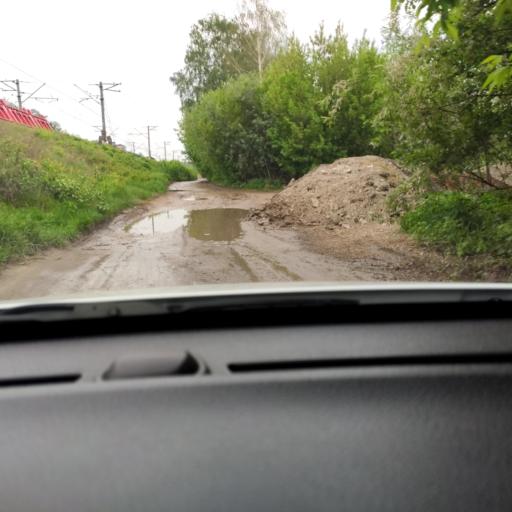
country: RU
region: Tatarstan
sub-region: Gorod Kazan'
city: Kazan
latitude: 55.8466
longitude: 49.1714
